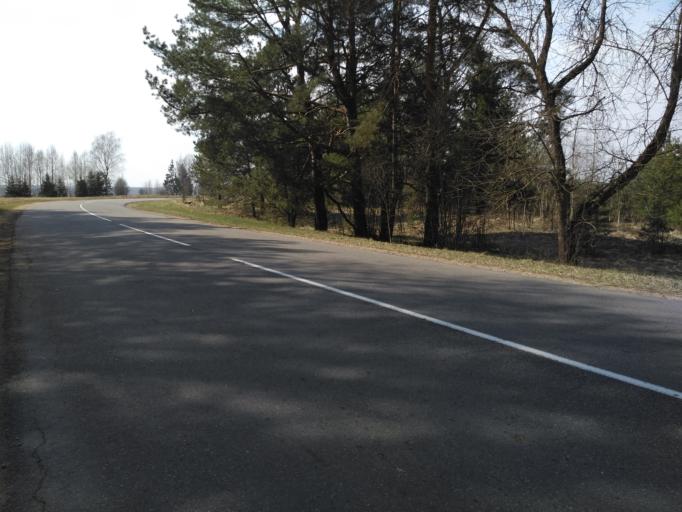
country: BY
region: Minsk
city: Zamostochcha
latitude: 53.8947
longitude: 27.9276
